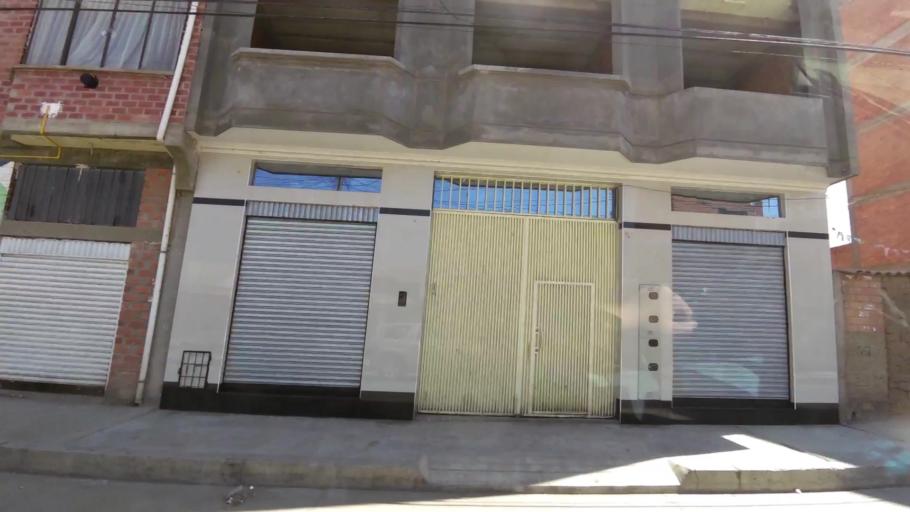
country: BO
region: La Paz
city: La Paz
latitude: -16.5277
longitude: -68.1582
